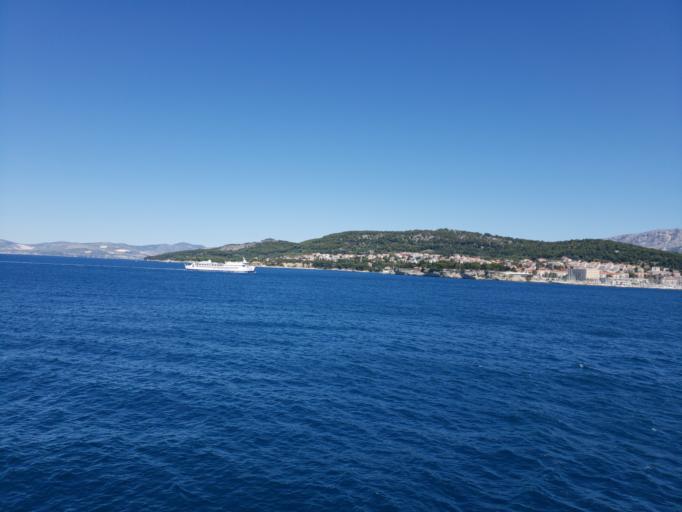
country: HR
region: Splitsko-Dalmatinska
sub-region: Grad Split
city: Split
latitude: 43.4930
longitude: 16.4335
